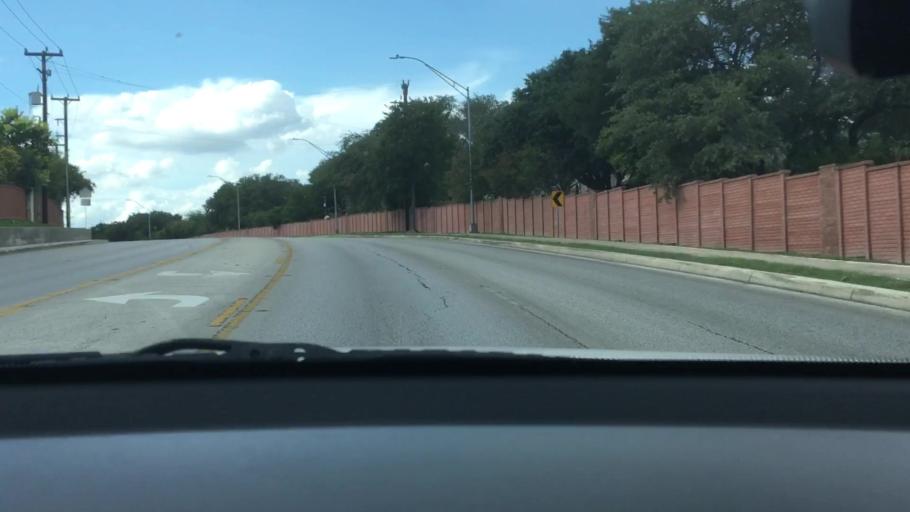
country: US
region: Texas
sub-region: Bexar County
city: Live Oak
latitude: 29.5910
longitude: -98.3971
